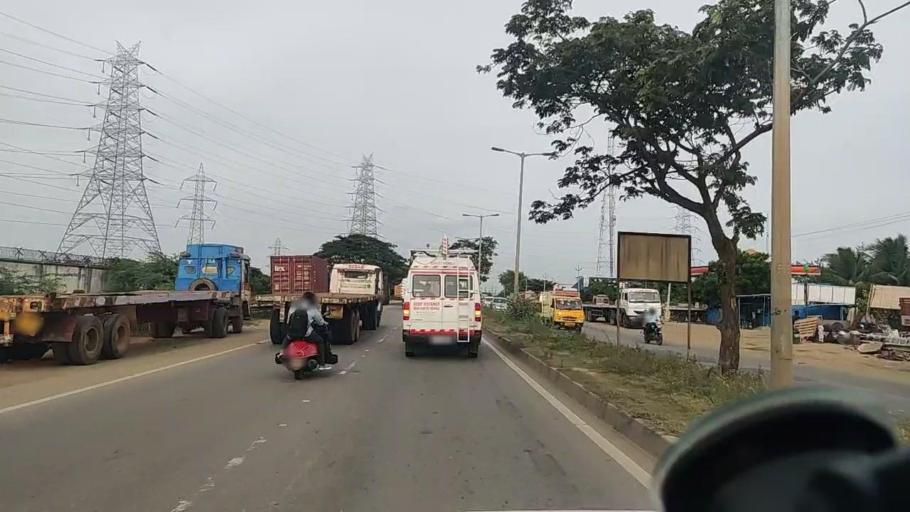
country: IN
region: Tamil Nadu
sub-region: Thiruvallur
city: Manali
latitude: 13.1812
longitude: 80.2608
